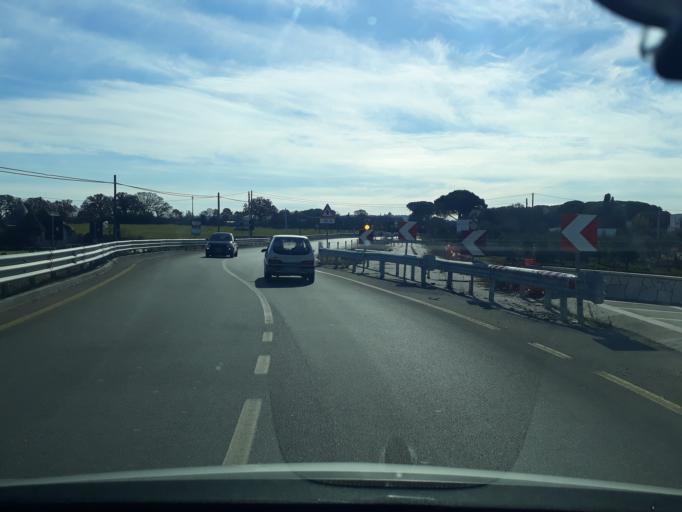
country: IT
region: Apulia
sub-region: Provincia di Bari
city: Locorotondo
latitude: 40.7368
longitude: 17.3326
